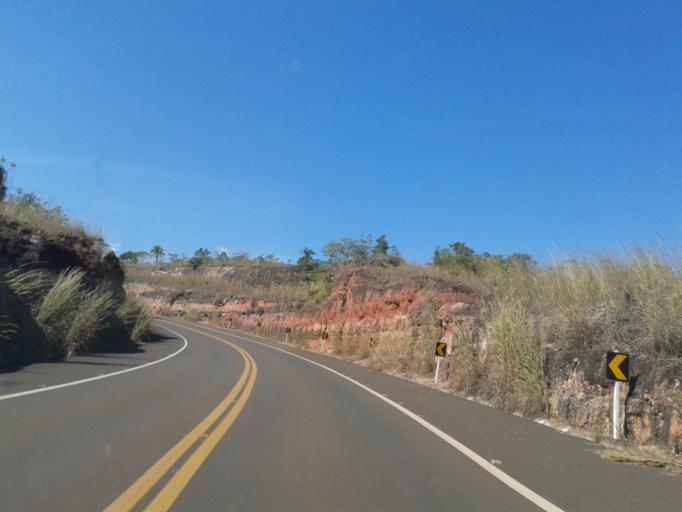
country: BR
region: Minas Gerais
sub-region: Campina Verde
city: Campina Verde
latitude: -19.4066
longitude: -49.5994
